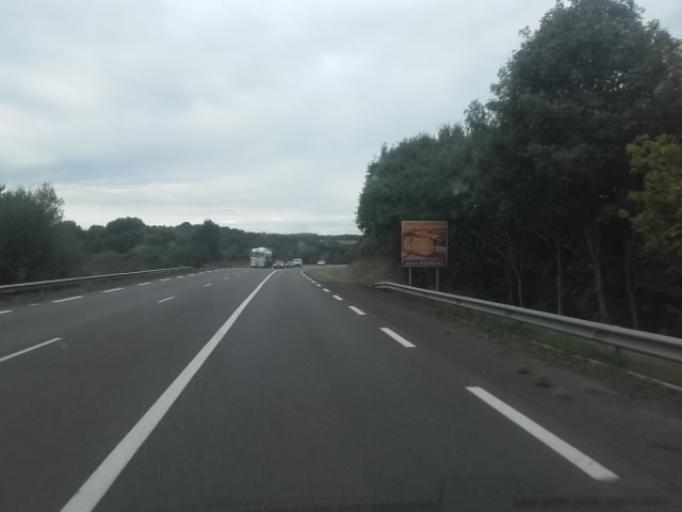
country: FR
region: Brittany
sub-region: Departement des Cotes-d'Armor
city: Lantic
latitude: 48.5685
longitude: -2.8992
